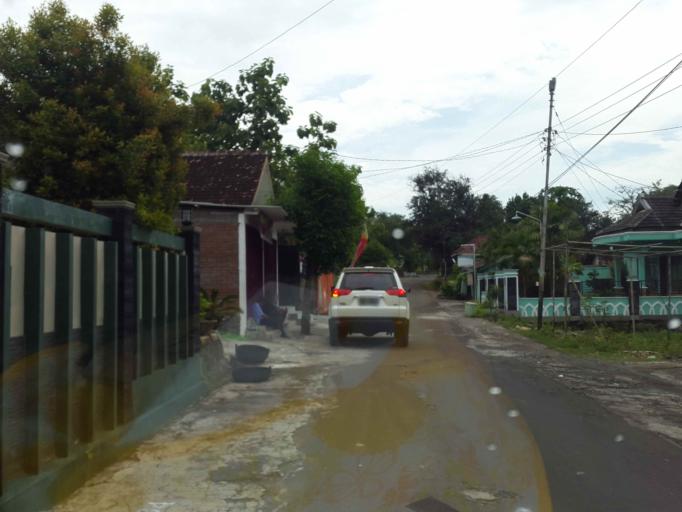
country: ID
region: Daerah Istimewa Yogyakarta
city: Wonosari
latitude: -7.9596
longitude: 110.6109
